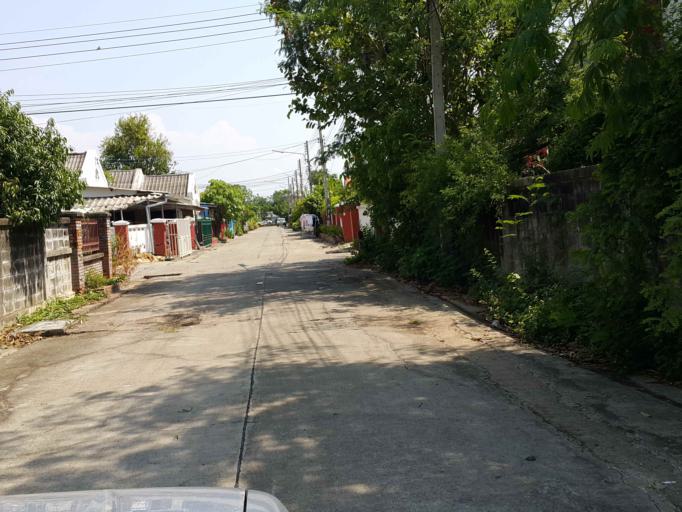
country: TH
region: Chiang Mai
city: Chiang Mai
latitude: 18.7504
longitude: 98.9580
